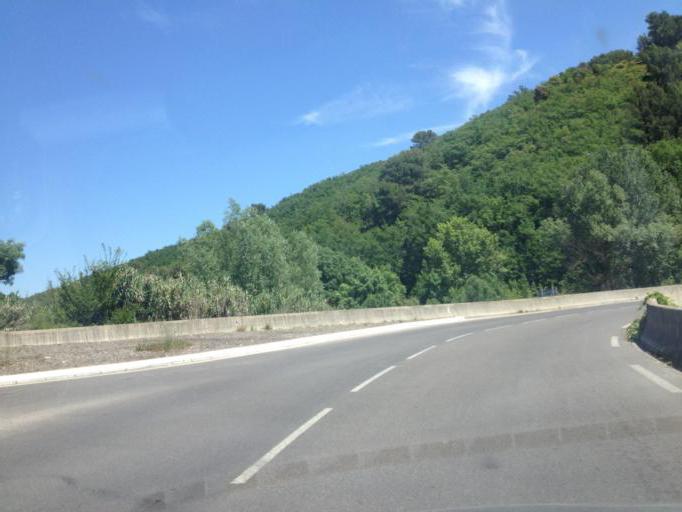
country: FR
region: Provence-Alpes-Cote d'Azur
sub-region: Departement du Vaucluse
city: Lauris
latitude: 43.7430
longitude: 5.3436
